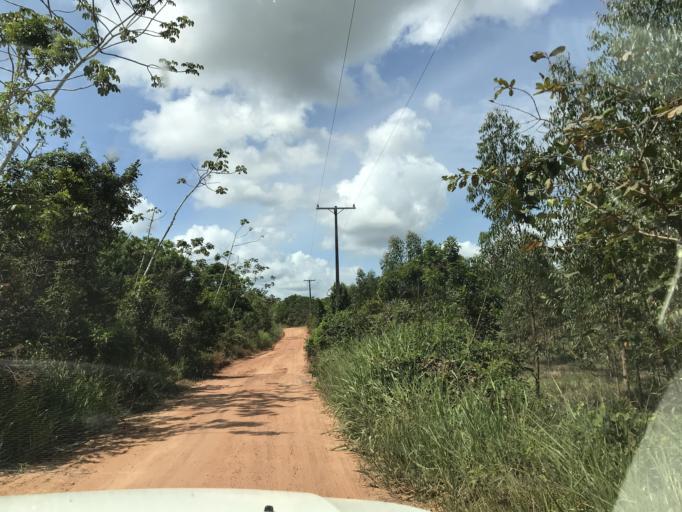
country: BR
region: Bahia
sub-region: Entre Rios
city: Entre Rios
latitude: -12.2203
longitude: -38.0842
